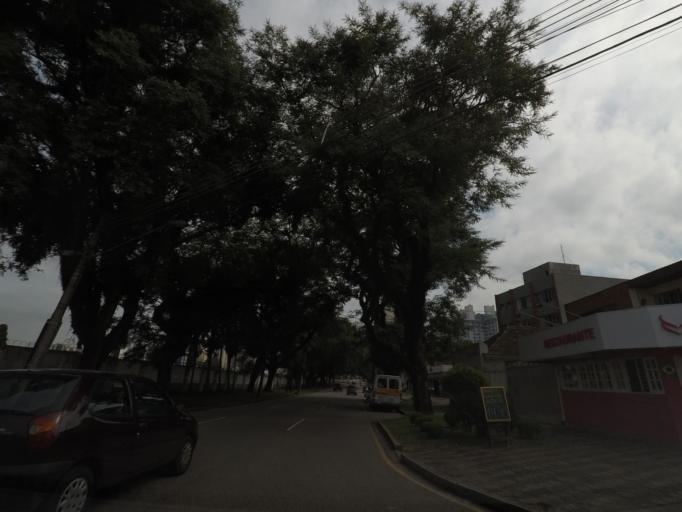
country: BR
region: Parana
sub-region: Curitiba
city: Curitiba
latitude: -25.4532
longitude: -49.2816
